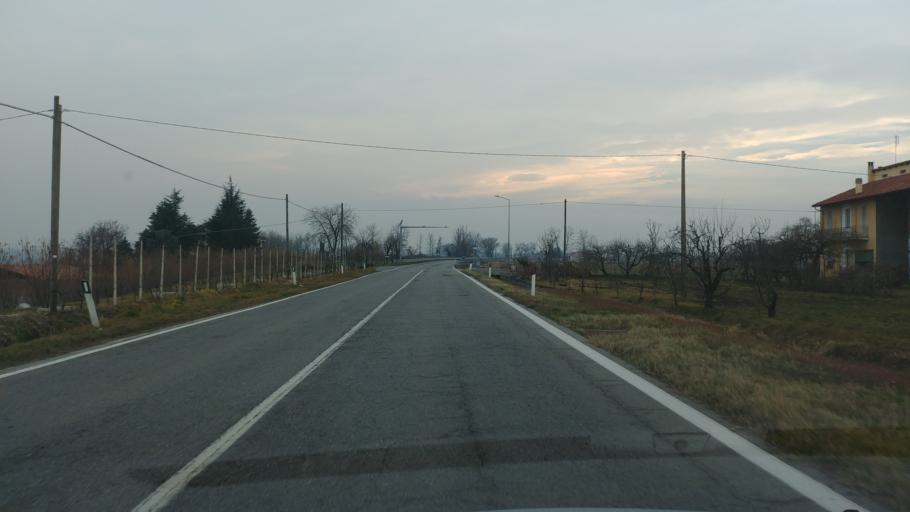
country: IT
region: Piedmont
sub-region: Provincia di Cuneo
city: Montanera
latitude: 44.4969
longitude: 7.6700
